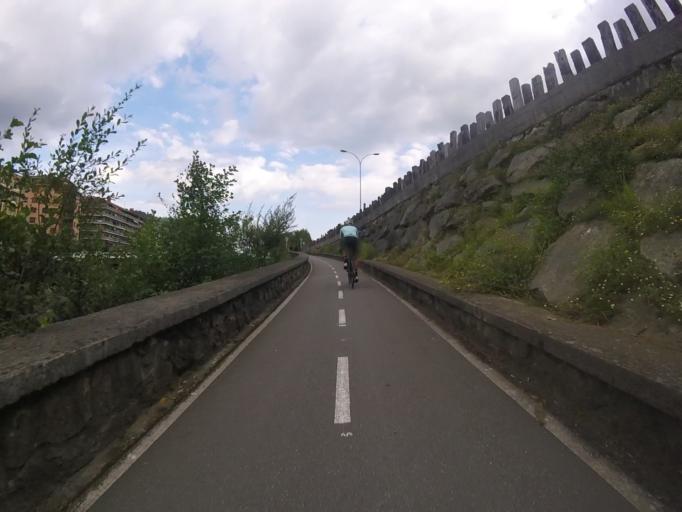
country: ES
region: Basque Country
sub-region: Provincia de Guipuzcoa
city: Tolosa
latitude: 43.1342
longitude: -2.0729
